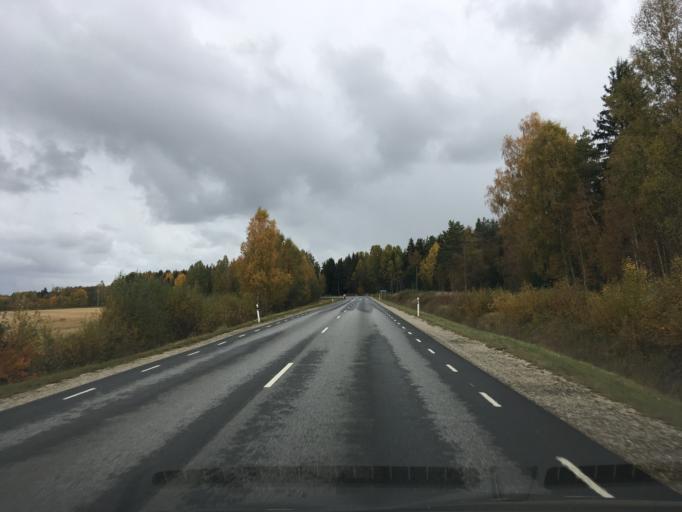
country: EE
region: Harju
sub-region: Anija vald
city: Kehra
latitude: 59.3160
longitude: 25.3437
